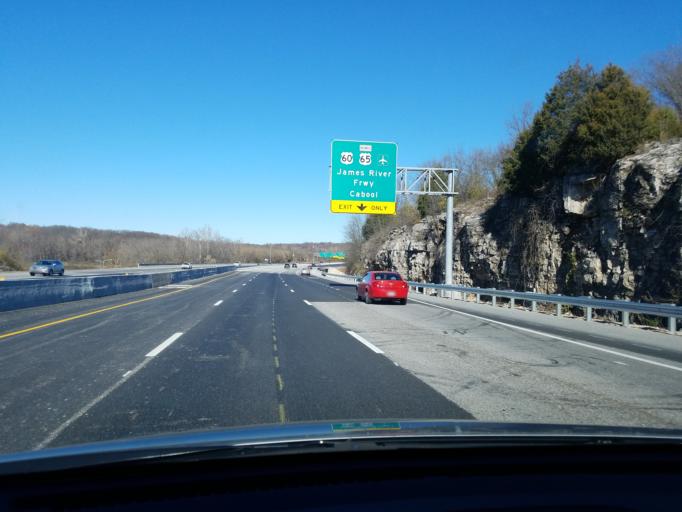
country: US
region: Missouri
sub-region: Christian County
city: Nixa
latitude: 37.1181
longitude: -93.2344
